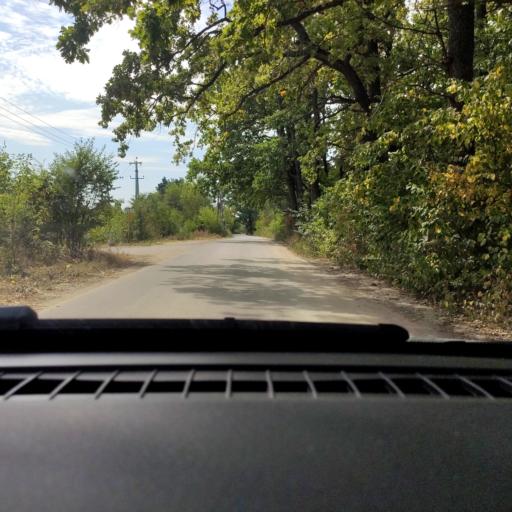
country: RU
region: Voronezj
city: Pridonskoy
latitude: 51.7428
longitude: 39.0721
